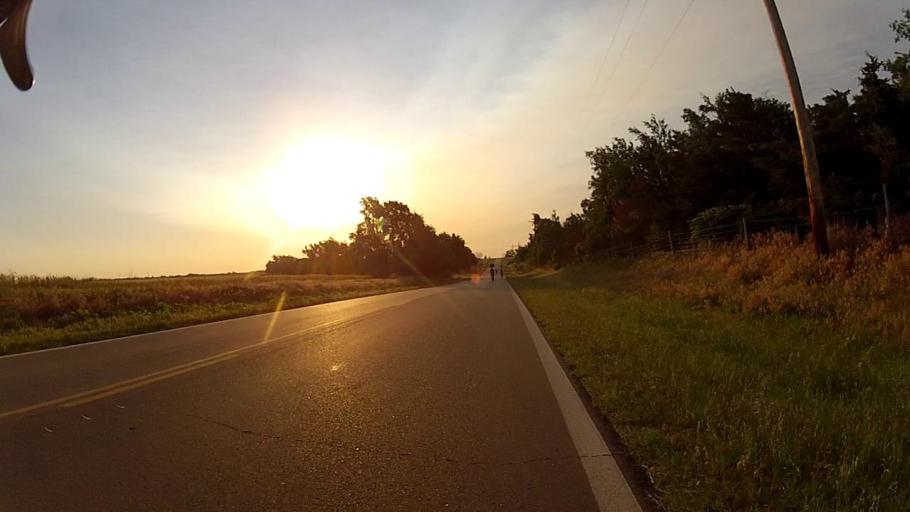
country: US
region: Kansas
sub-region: Harper County
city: Anthony
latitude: 37.1526
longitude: -97.9536
